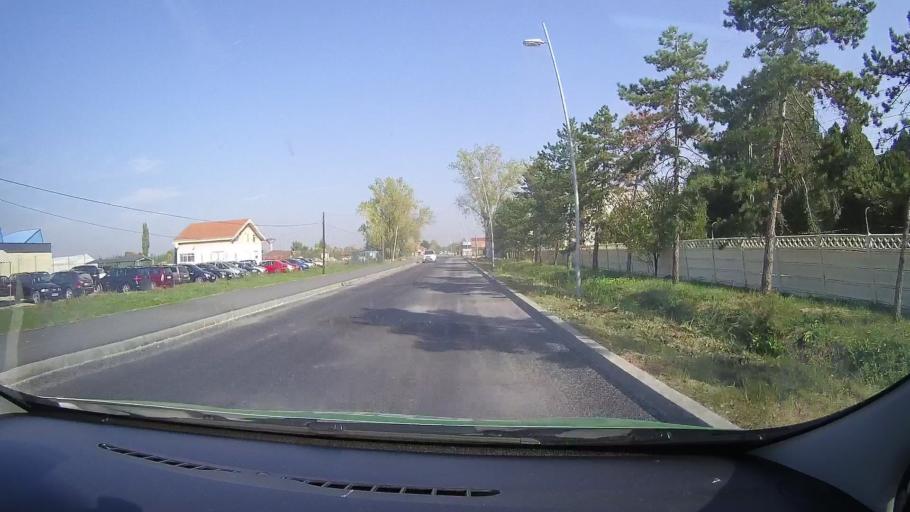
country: RO
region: Bihor
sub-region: Municipiul Salonta
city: Salonta
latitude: 46.7921
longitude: 21.6643
